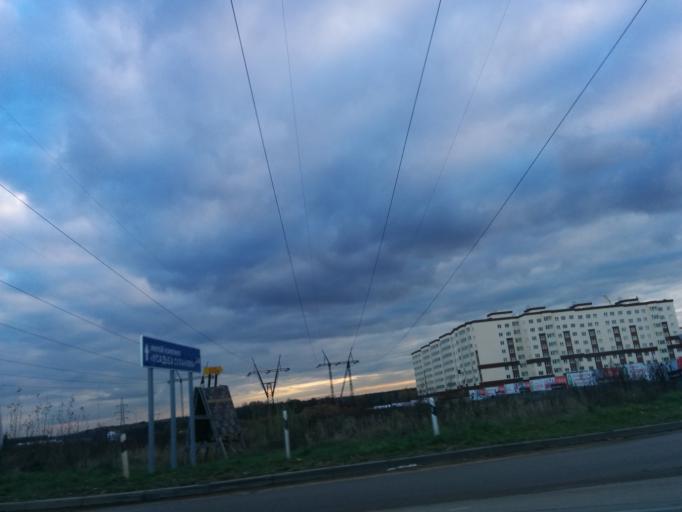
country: RU
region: Moscow
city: Zagor'ye
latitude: 55.5372
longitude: 37.6391
